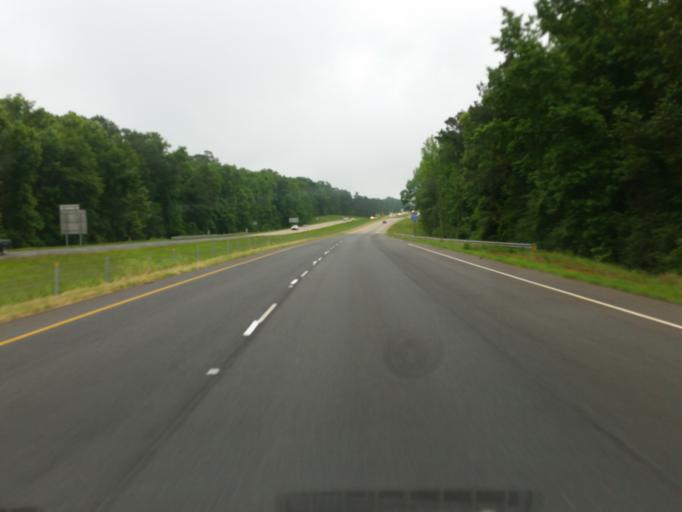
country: US
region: Louisiana
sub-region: Bienville Parish
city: Arcadia
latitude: 32.5632
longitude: -93.0505
